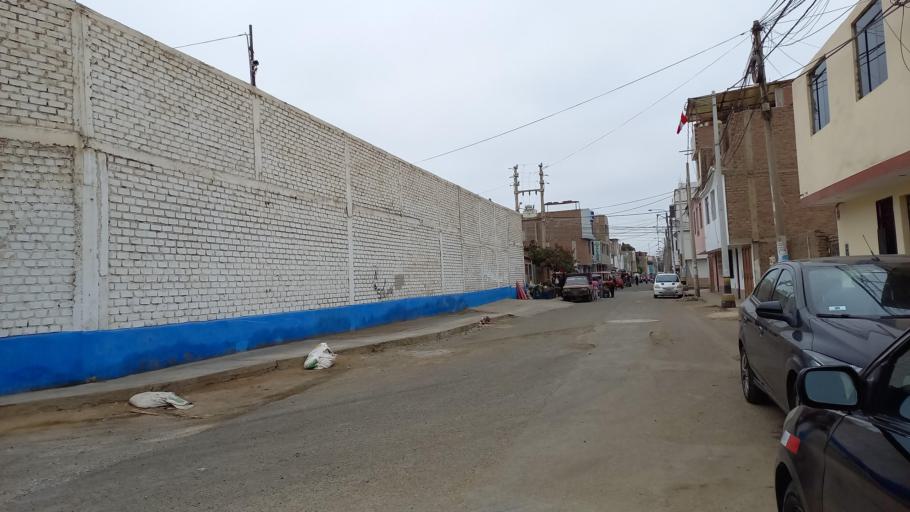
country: PE
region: La Libertad
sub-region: Provincia de Trujillo
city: Trujillo
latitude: -8.1051
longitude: -79.0438
